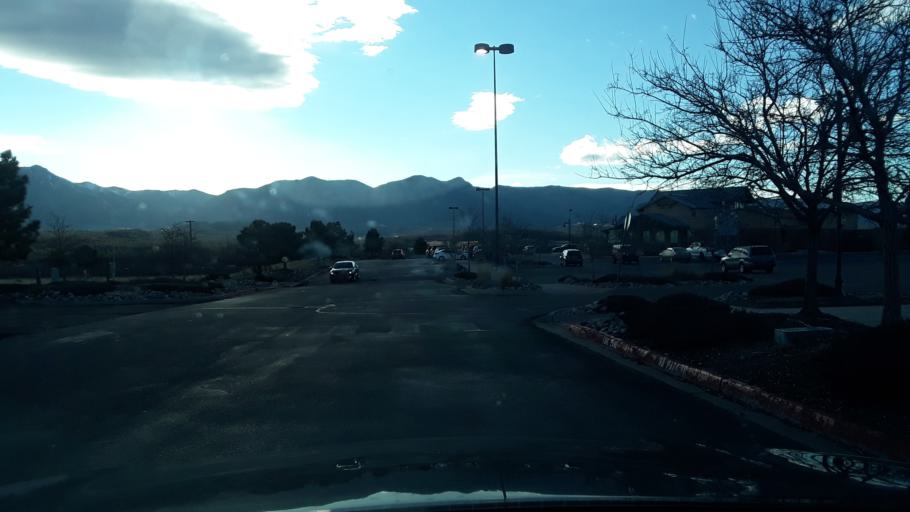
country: US
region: Colorado
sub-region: El Paso County
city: Air Force Academy
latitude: 38.9931
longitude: -104.8105
